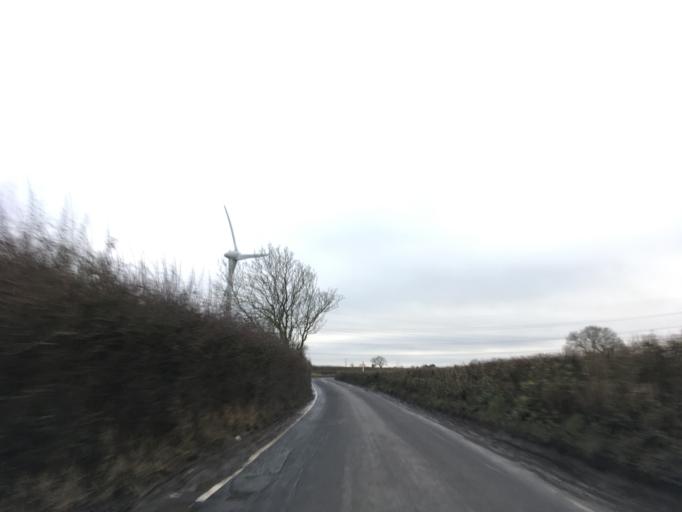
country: GB
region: England
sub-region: South Gloucestershire
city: Alveston
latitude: 51.5603
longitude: -2.5109
